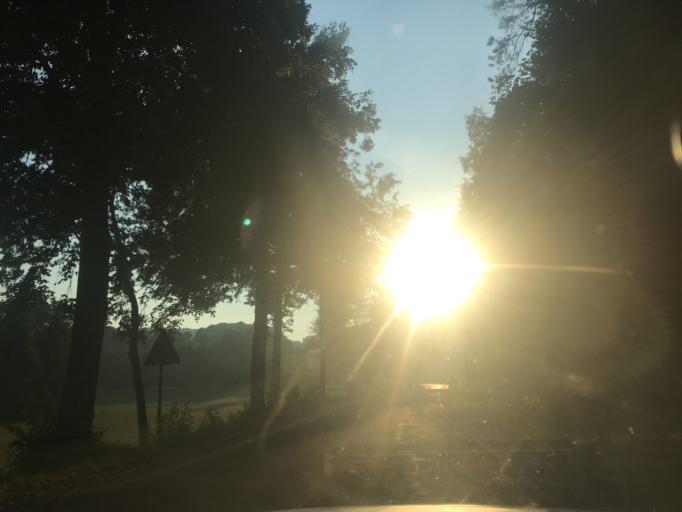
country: DE
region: Bavaria
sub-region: Upper Franconia
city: Pegnitz
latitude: 49.7397
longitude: 11.5535
